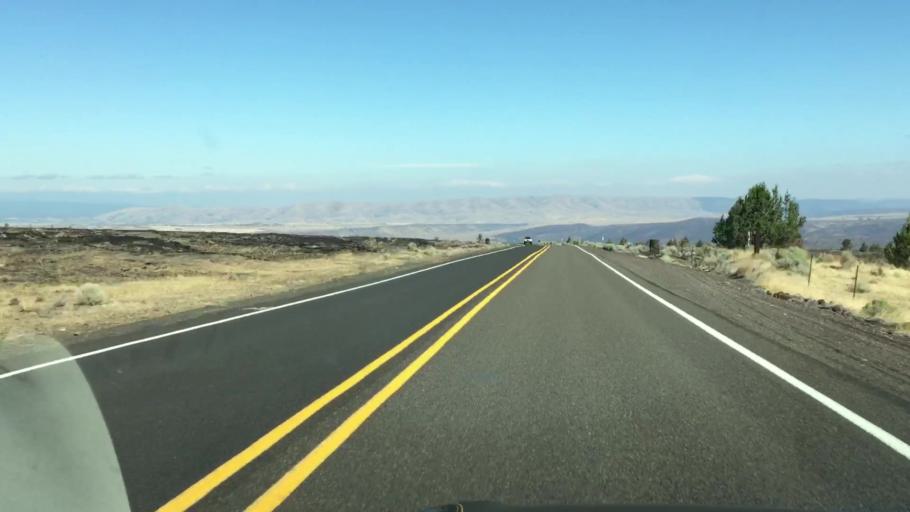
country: US
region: Oregon
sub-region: Jefferson County
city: Warm Springs
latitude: 45.0888
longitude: -121.0275
